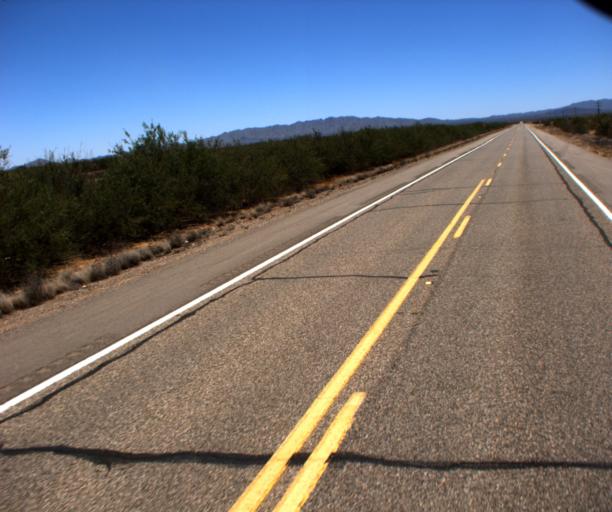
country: US
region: Arizona
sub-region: Pima County
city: Ajo
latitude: 32.1901
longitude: -112.4103
